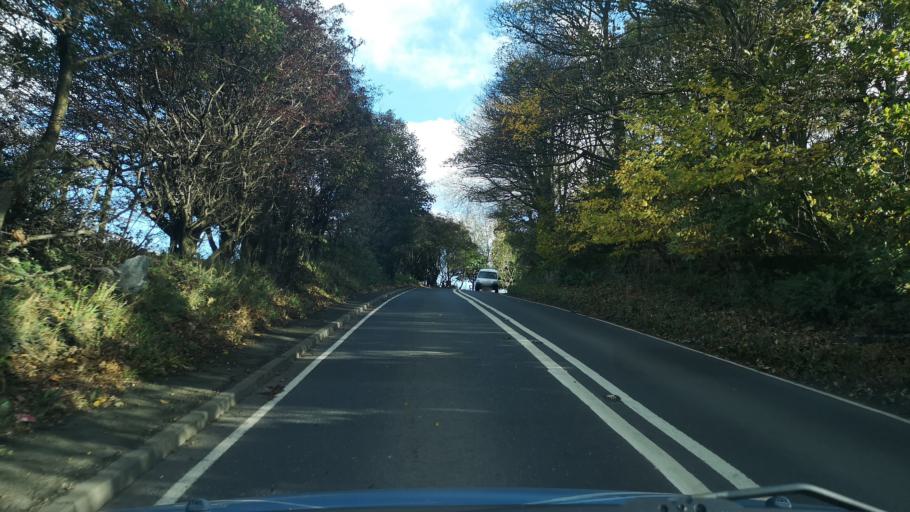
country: GB
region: England
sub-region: Kirklees
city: Mirfield
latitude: 53.6506
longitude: -1.6867
